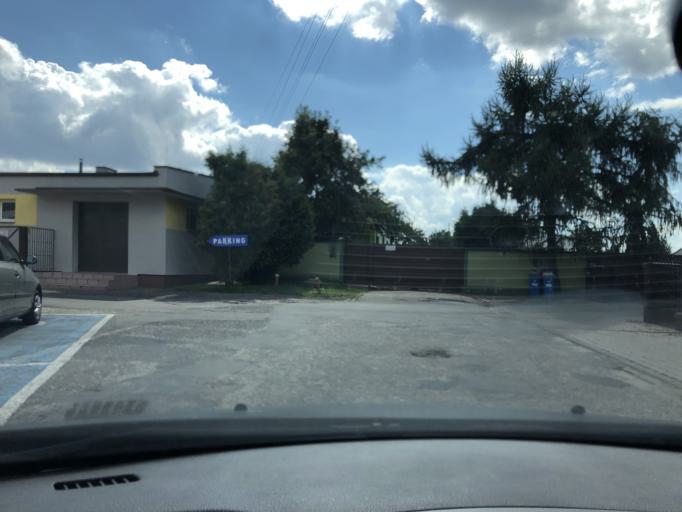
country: PL
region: Lodz Voivodeship
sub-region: Powiat wieruszowski
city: Wieruszow
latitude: 51.2942
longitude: 18.1643
